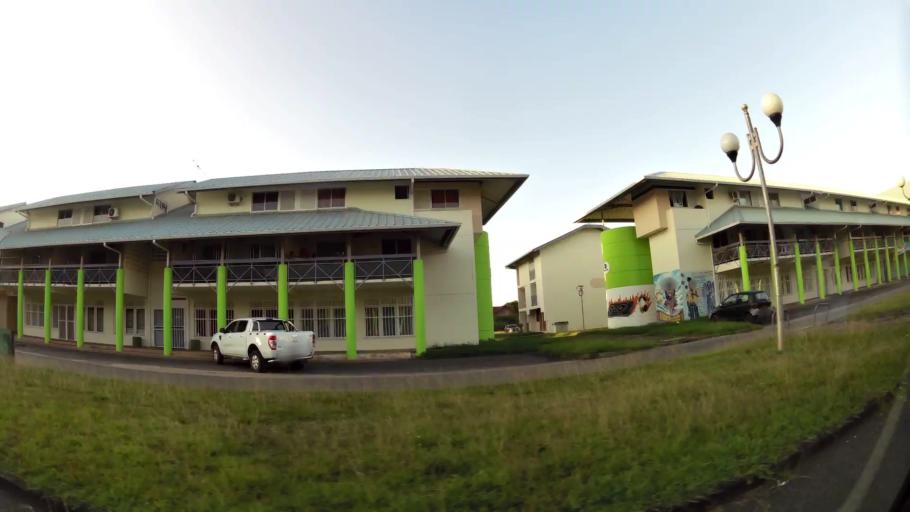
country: GF
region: Guyane
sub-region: Guyane
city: Cayenne
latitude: 4.9262
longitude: -52.3007
